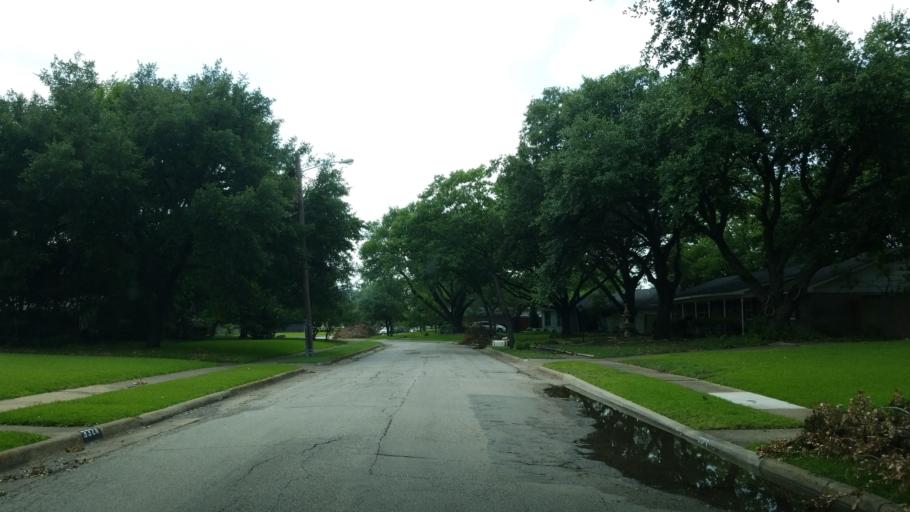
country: US
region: Texas
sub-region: Dallas County
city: Farmers Branch
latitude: 32.9077
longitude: -96.8655
